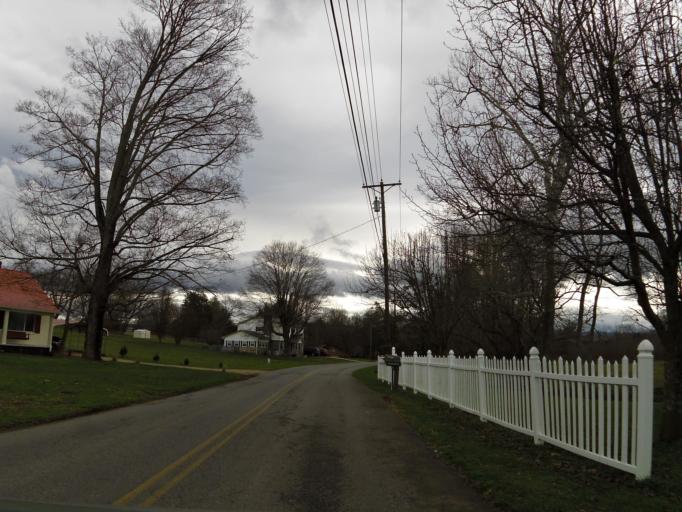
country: US
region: Tennessee
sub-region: Greene County
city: Tusculum
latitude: 36.1923
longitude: -82.7366
